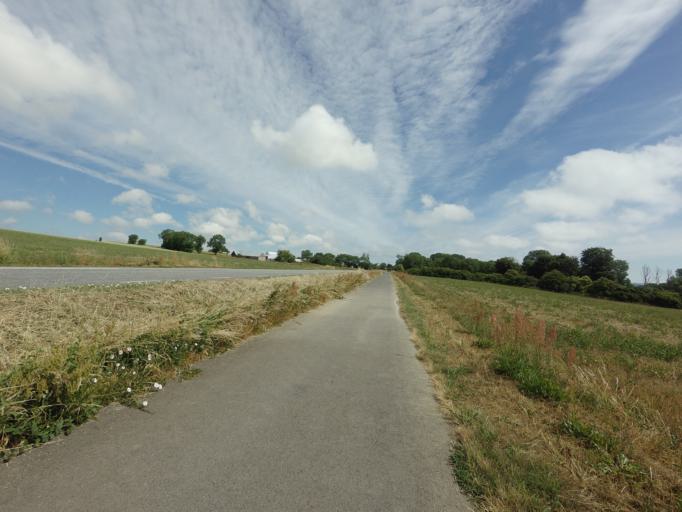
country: SE
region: Skane
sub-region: Simrishamns Kommun
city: Simrishamn
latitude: 55.4952
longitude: 14.3154
